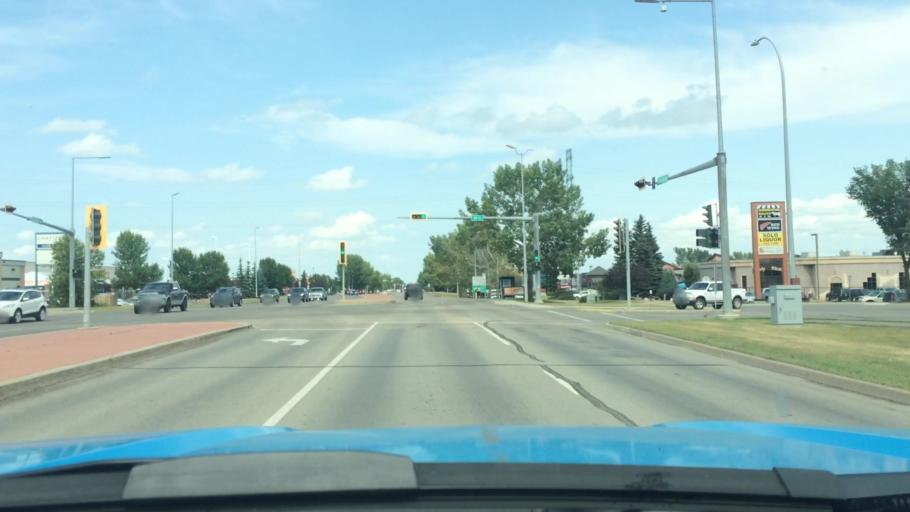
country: CA
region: Alberta
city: Red Deer
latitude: 52.2350
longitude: -113.8139
